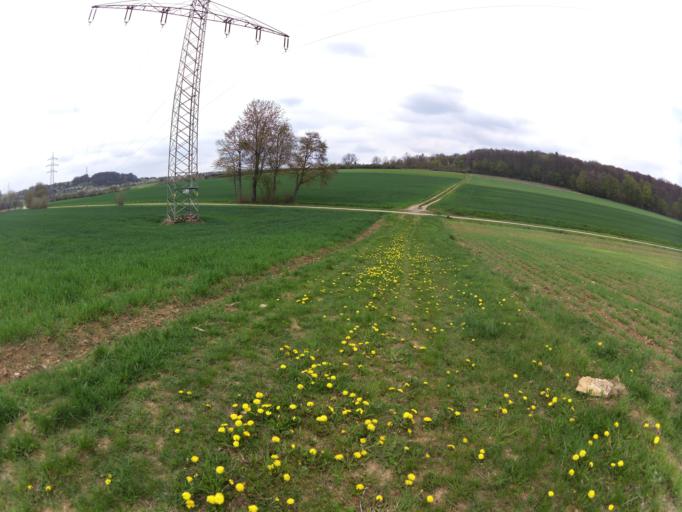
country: DE
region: Bavaria
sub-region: Regierungsbezirk Unterfranken
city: Hettstadt
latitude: 49.8137
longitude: 9.8076
